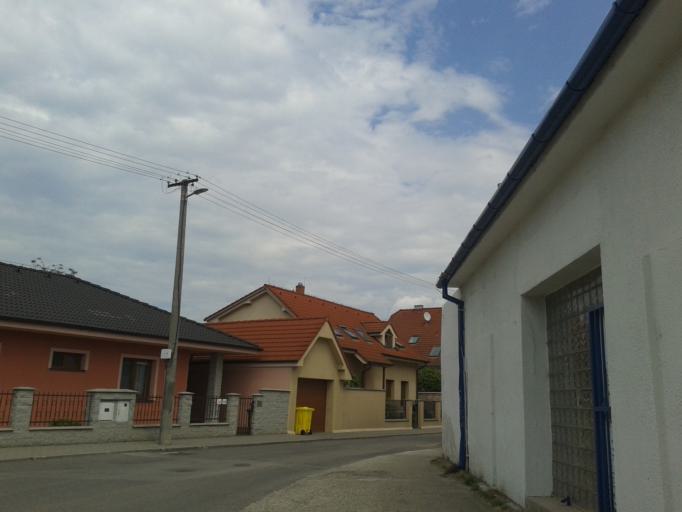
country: SK
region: Bratislavsky
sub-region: Okres Malacky
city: Malacky
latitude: 48.4318
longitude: 17.0208
